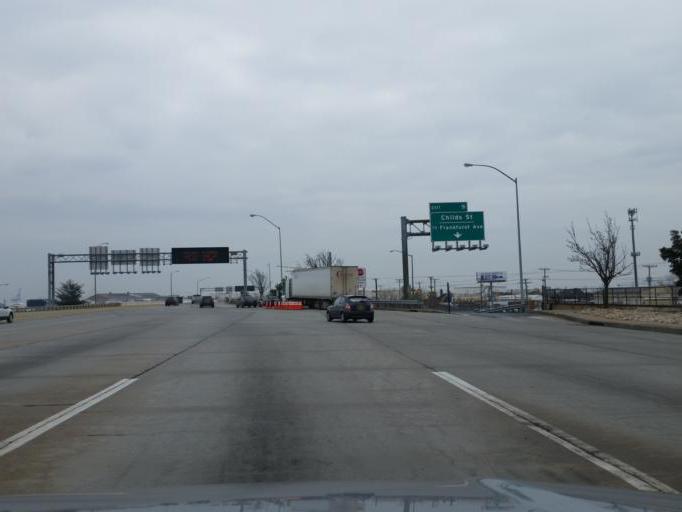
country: US
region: Maryland
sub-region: Anne Arundel County
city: Brooklyn Park
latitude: 39.2408
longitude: -76.5871
